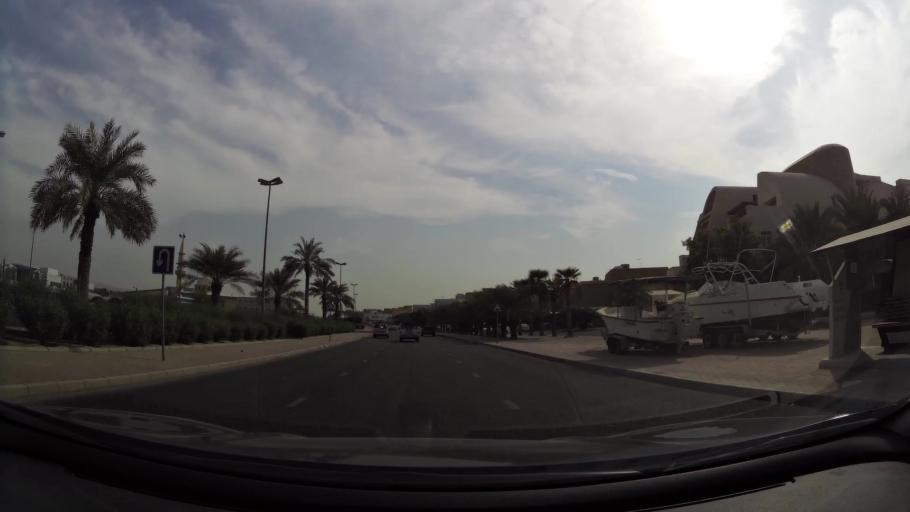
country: KW
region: Al Asimah
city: Ash Shamiyah
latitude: 29.3283
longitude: 47.9618
